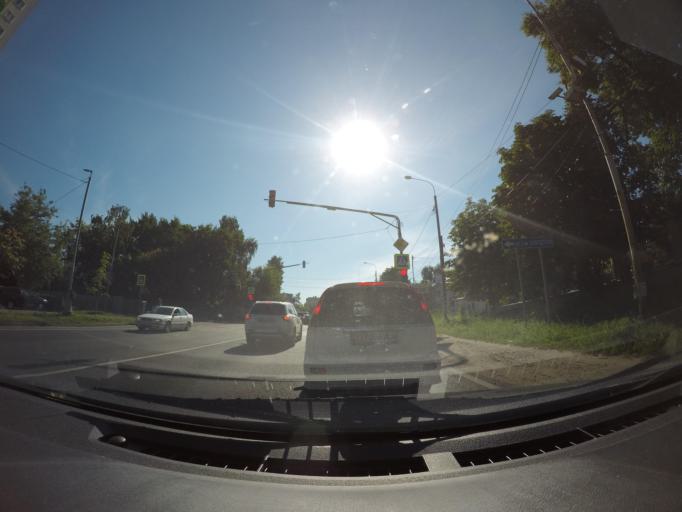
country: RU
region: Moskovskaya
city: Kraskovo
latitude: 55.6594
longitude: 37.9759
